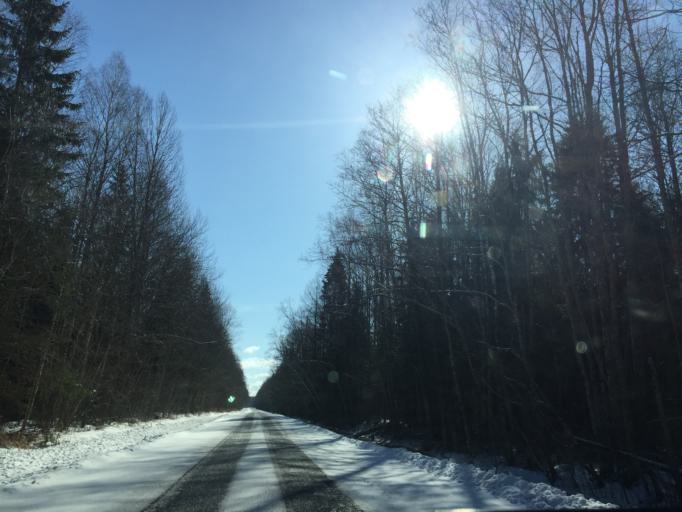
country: LV
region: Salacgrivas
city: Ainazi
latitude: 58.0029
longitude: 24.5151
